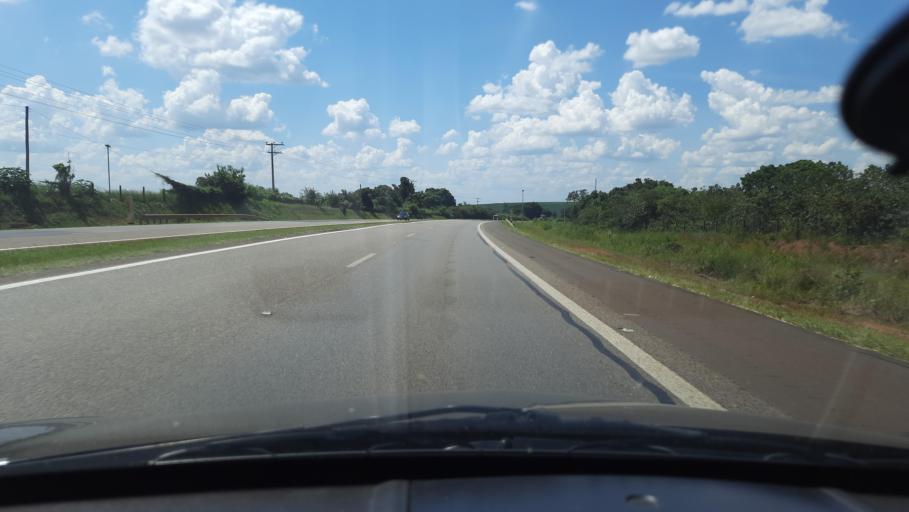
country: BR
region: Sao Paulo
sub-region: Casa Branca
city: Casa Branca
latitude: -21.7079
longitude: -47.0857
